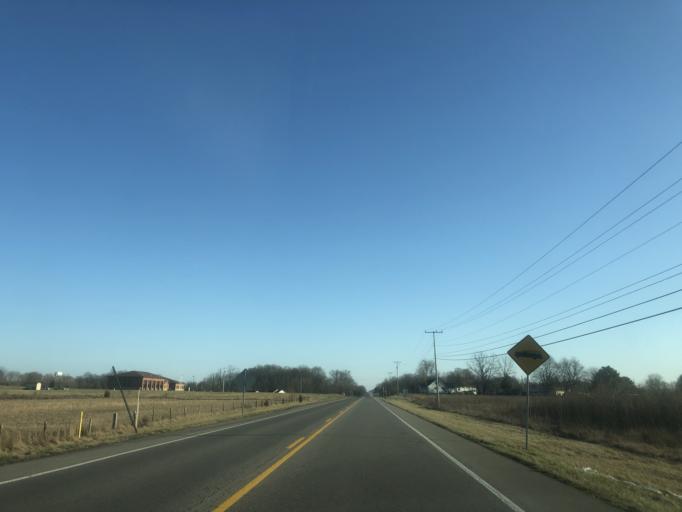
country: US
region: Tennessee
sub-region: Sumner County
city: Portland
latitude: 36.6185
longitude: -86.5509
